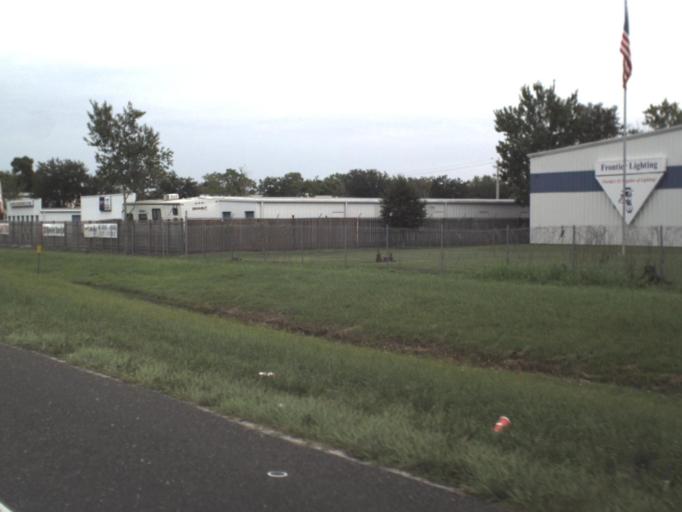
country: US
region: Florida
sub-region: Manatee County
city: Samoset
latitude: 27.4310
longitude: -82.5303
